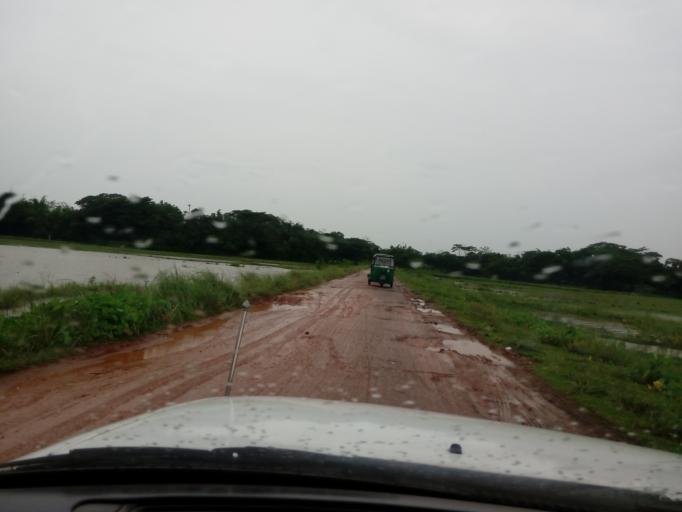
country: BD
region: Sylhet
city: Sylhet
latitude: 24.9631
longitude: 91.7949
